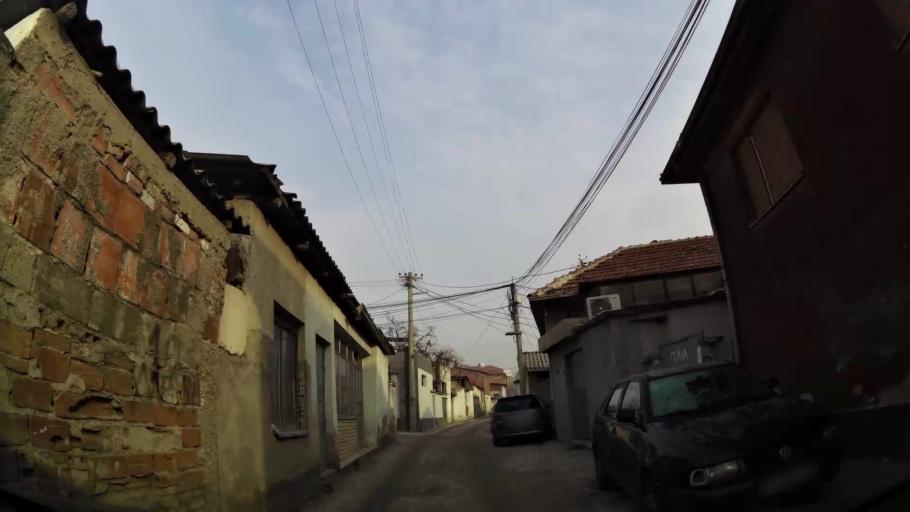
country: MK
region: Cair
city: Cair
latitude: 42.0192
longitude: 21.4385
